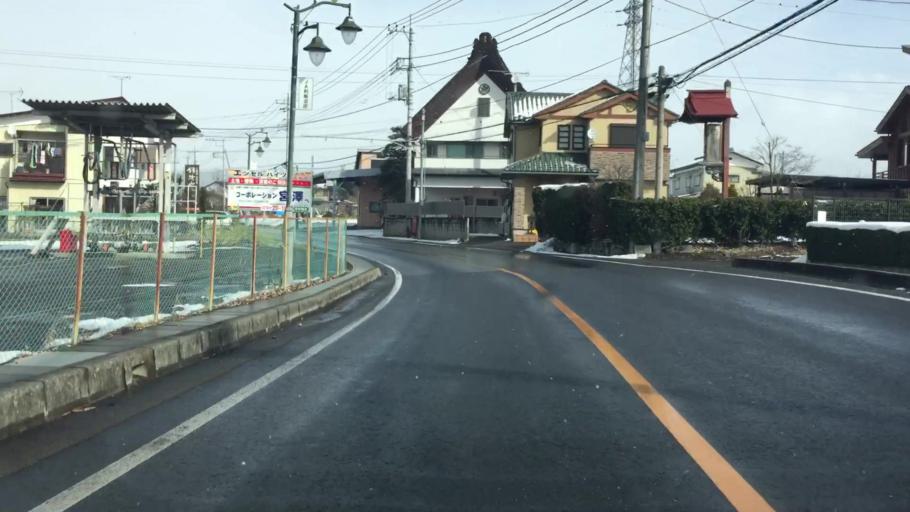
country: JP
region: Gunma
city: Numata
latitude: 36.6572
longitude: 139.0763
